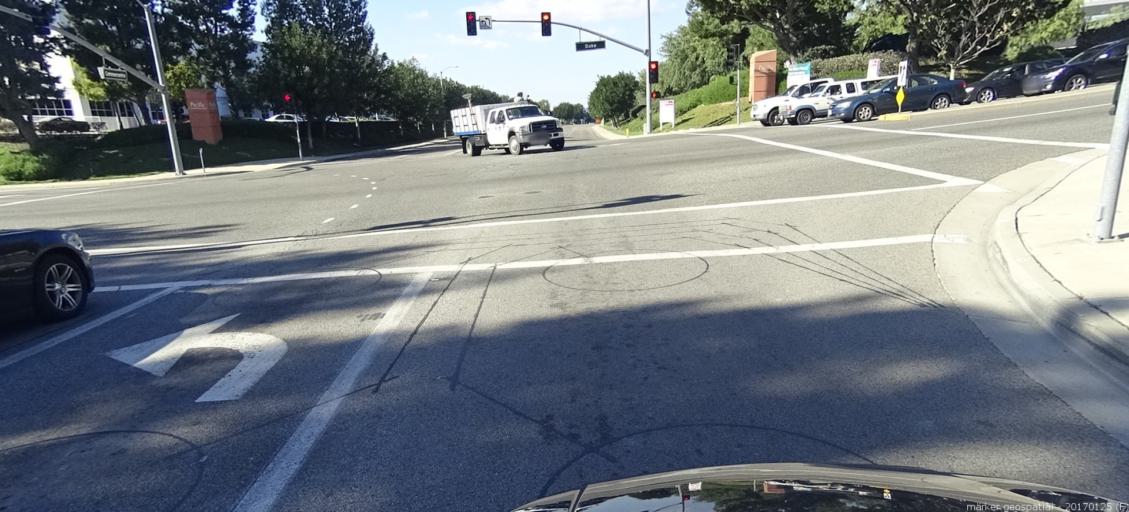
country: US
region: California
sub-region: Orange County
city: Lake Forest
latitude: 33.6653
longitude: -117.6859
